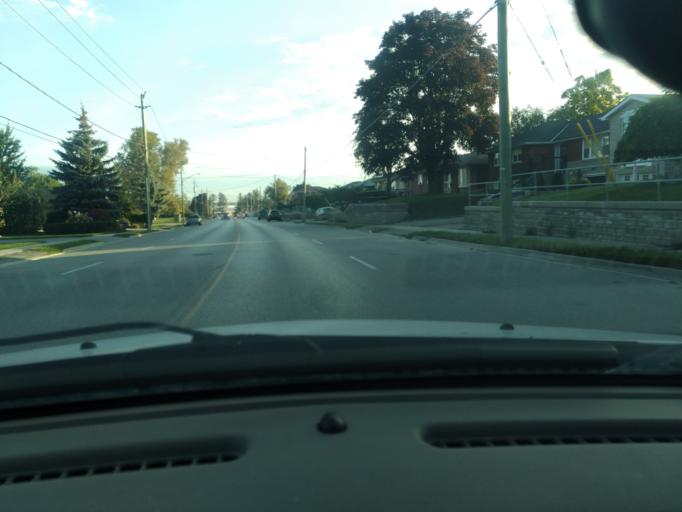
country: CA
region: Ontario
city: Bradford West Gwillimbury
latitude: 44.1069
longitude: -79.5650
